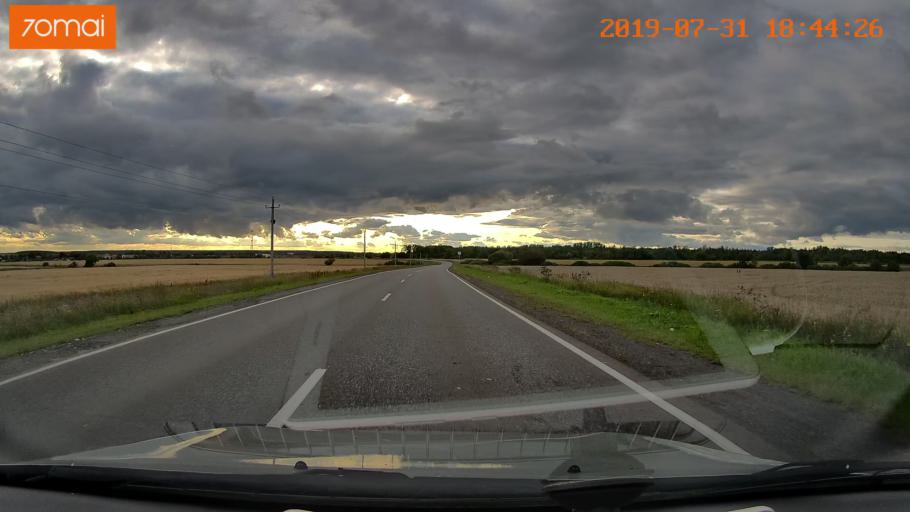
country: RU
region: Moskovskaya
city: Troitskoye
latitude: 55.2498
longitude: 38.5514
